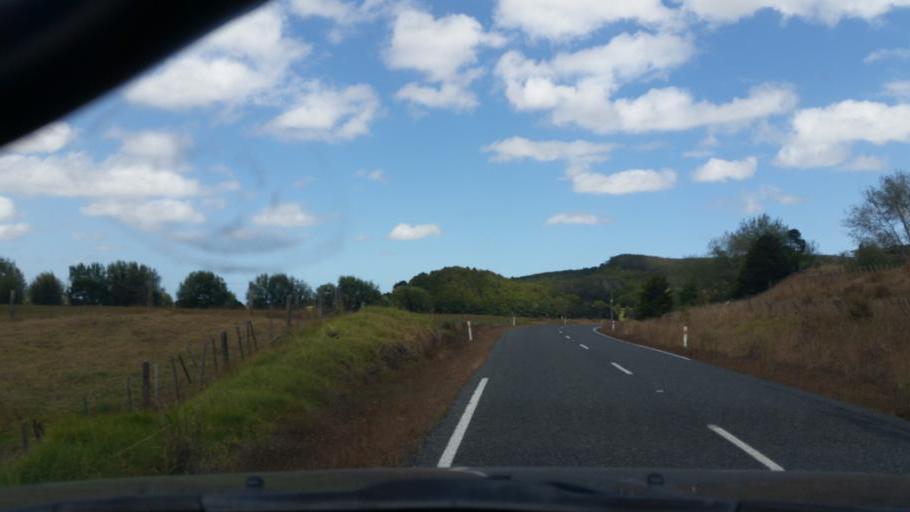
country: NZ
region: Northland
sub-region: Kaipara District
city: Dargaville
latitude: -35.8614
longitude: 173.8446
